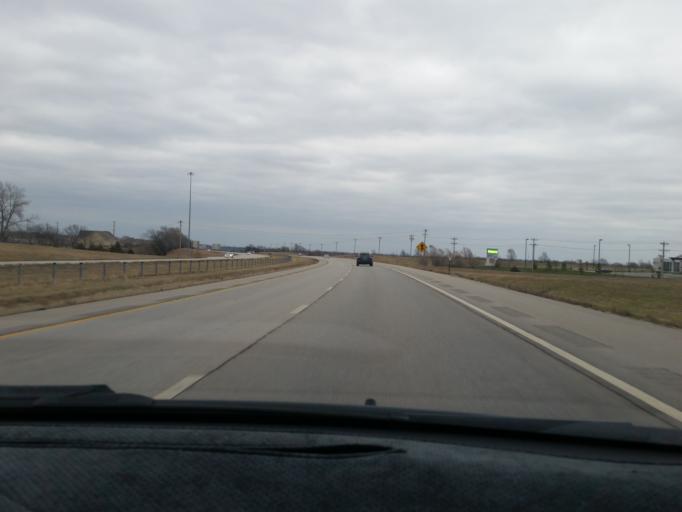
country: US
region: Kansas
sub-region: Douglas County
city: Eudora
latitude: 38.9298
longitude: -95.0938
